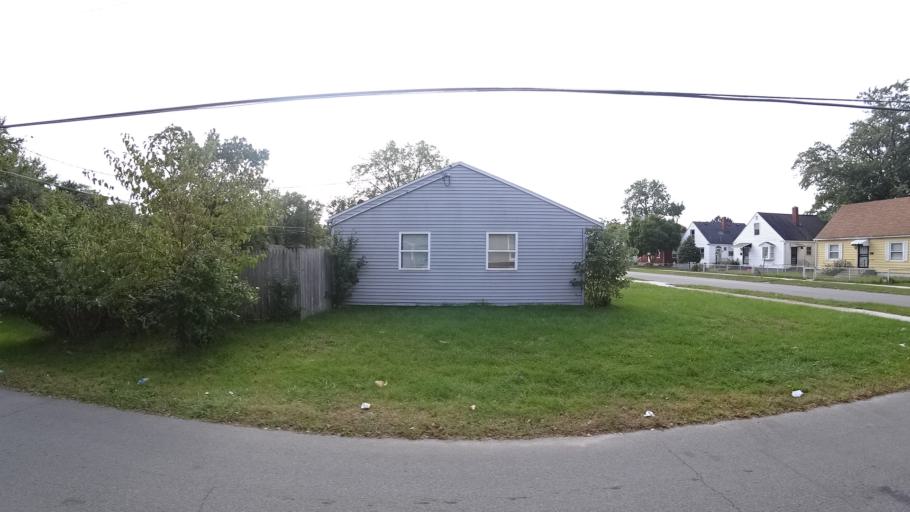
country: US
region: Indiana
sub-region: LaPorte County
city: Trail Creek
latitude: 41.7120
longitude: -86.8745
